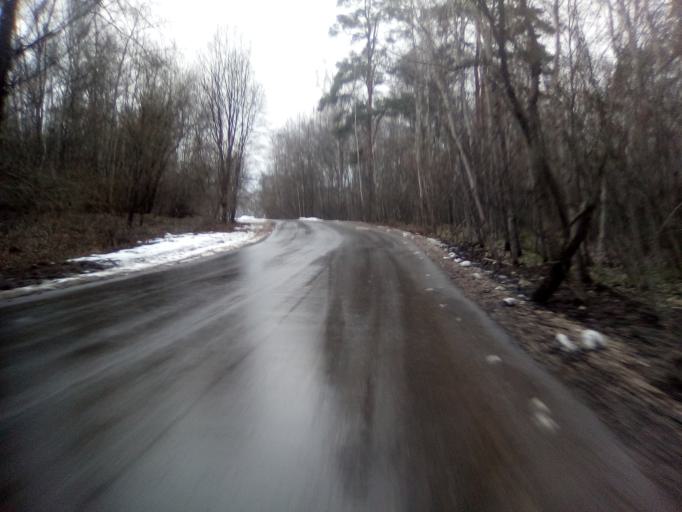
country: RU
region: Moskovskaya
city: Dubrovitsy
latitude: 55.5019
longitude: 37.4308
